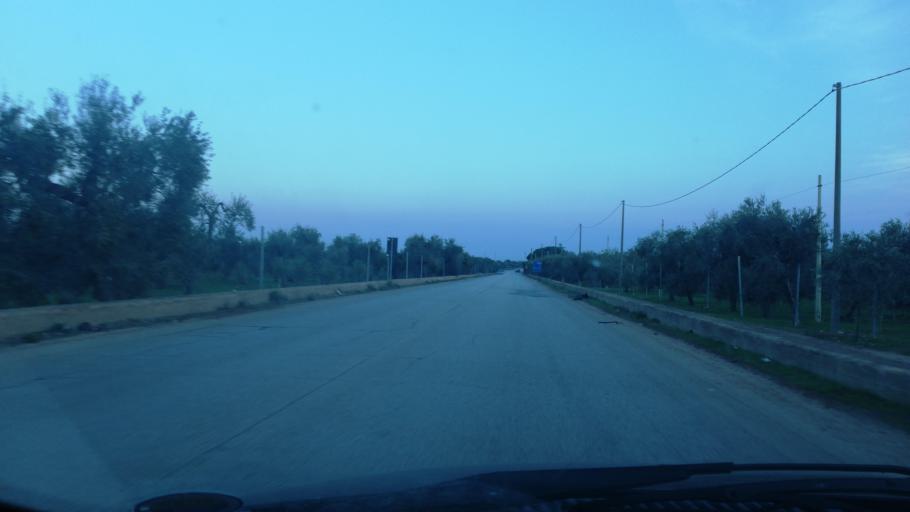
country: IT
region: Apulia
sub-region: Provincia di Bari
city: Bitonto
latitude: 41.1306
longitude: 16.7079
